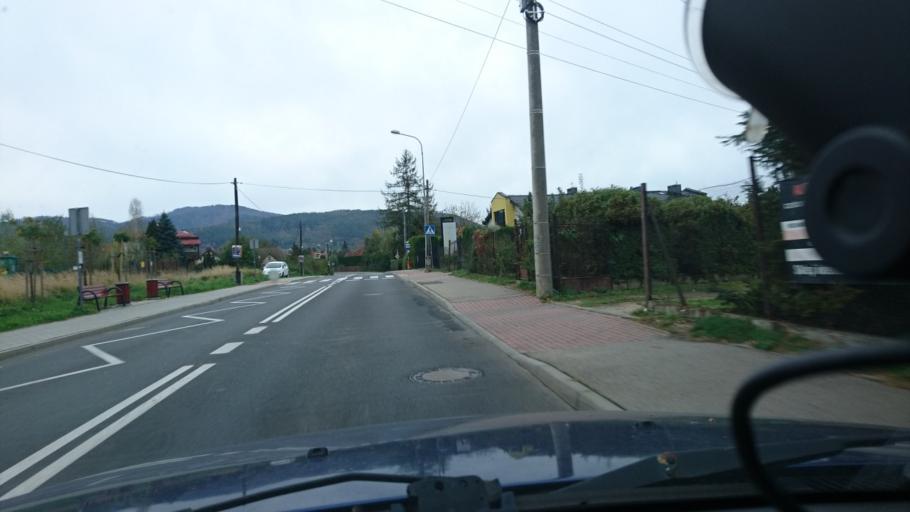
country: PL
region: Silesian Voivodeship
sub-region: Bielsko-Biala
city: Bielsko-Biala
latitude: 49.8008
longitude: 19.0222
